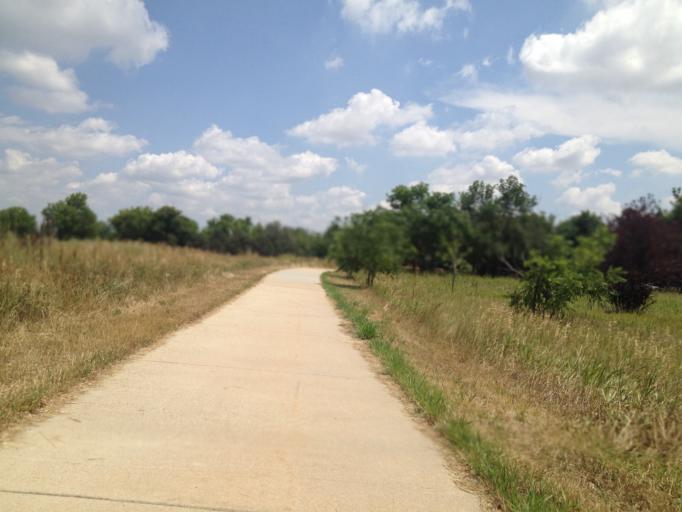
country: US
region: Colorado
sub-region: Boulder County
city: Louisville
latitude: 39.9657
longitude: -105.1488
